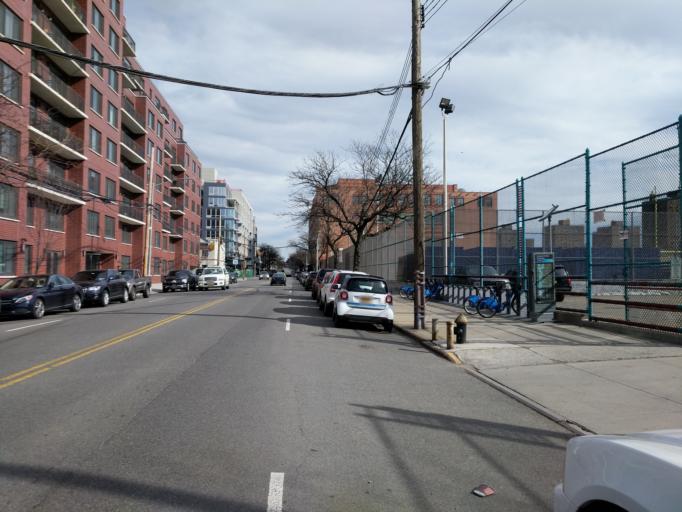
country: US
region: New York
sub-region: Queens County
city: Long Island City
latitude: 40.7670
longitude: -73.9349
